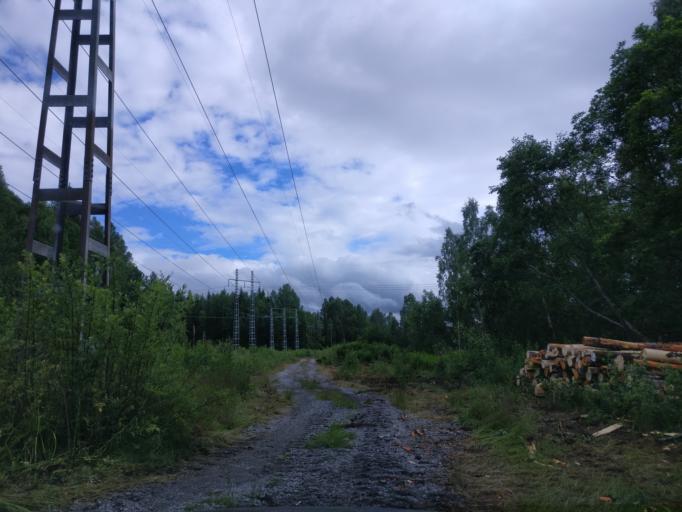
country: SE
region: Vaermland
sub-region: Hagfors Kommun
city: Ekshaerad
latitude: 60.0439
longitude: 13.5281
